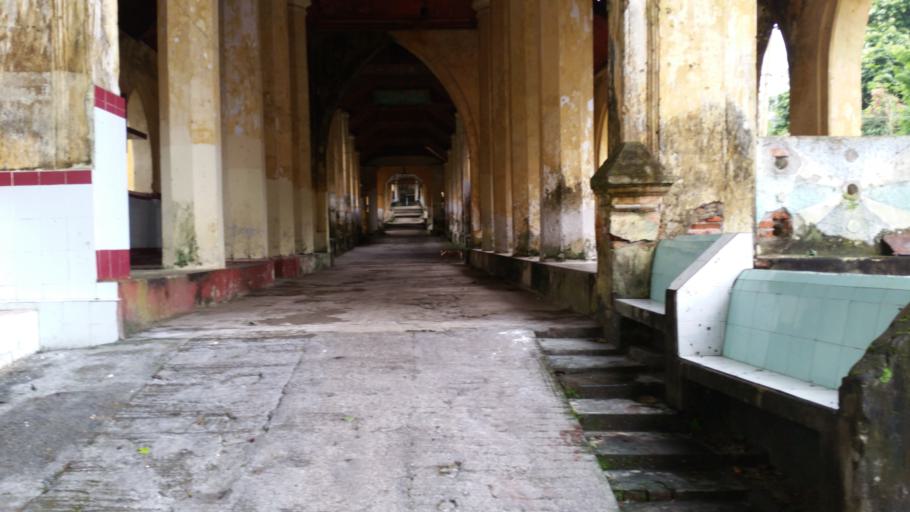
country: MM
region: Mon
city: Mawlamyine
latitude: 16.4883
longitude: 97.6248
